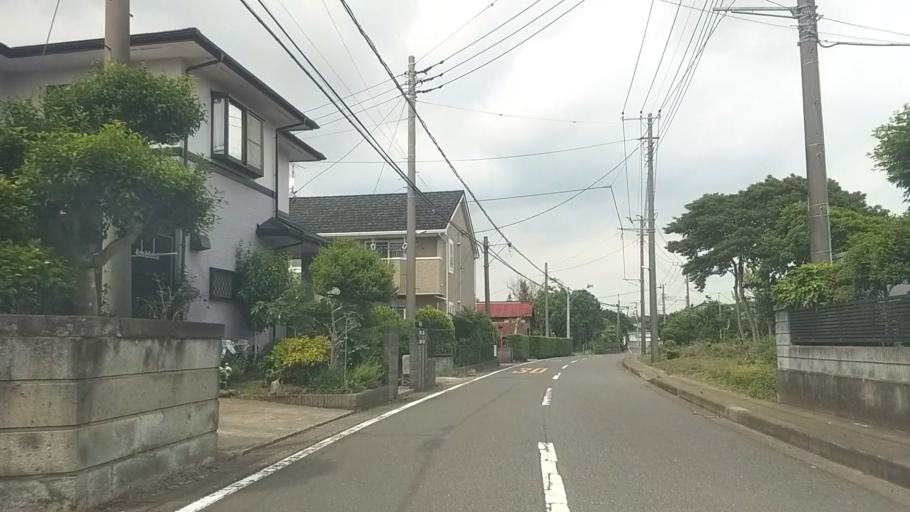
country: JP
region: Kanagawa
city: Chigasaki
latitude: 35.3915
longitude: 139.4145
